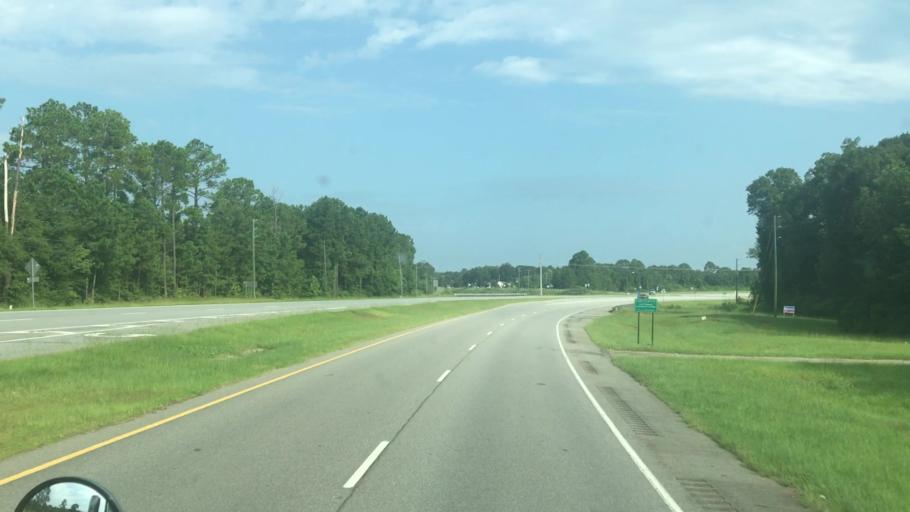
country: US
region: Georgia
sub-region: Early County
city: Blakely
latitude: 31.3551
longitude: -84.9214
